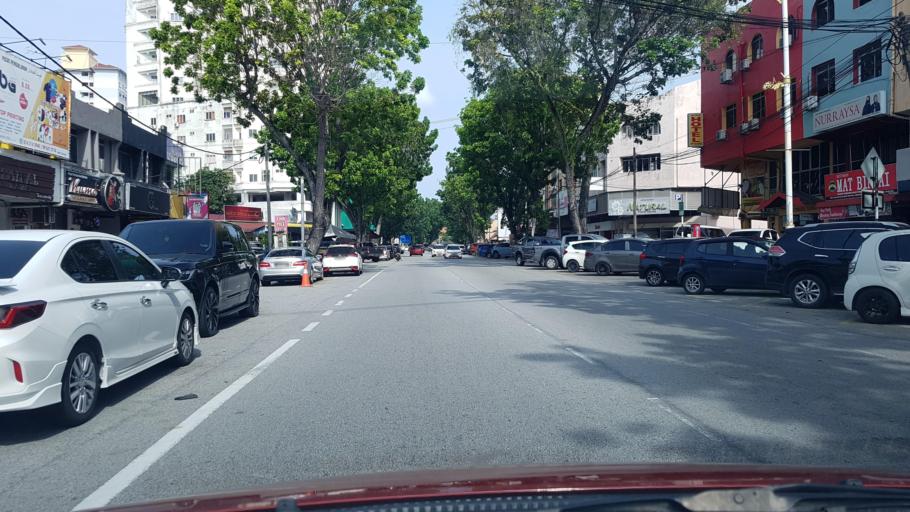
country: MY
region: Terengganu
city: Kuala Terengganu
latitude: 5.3316
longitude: 103.1439
